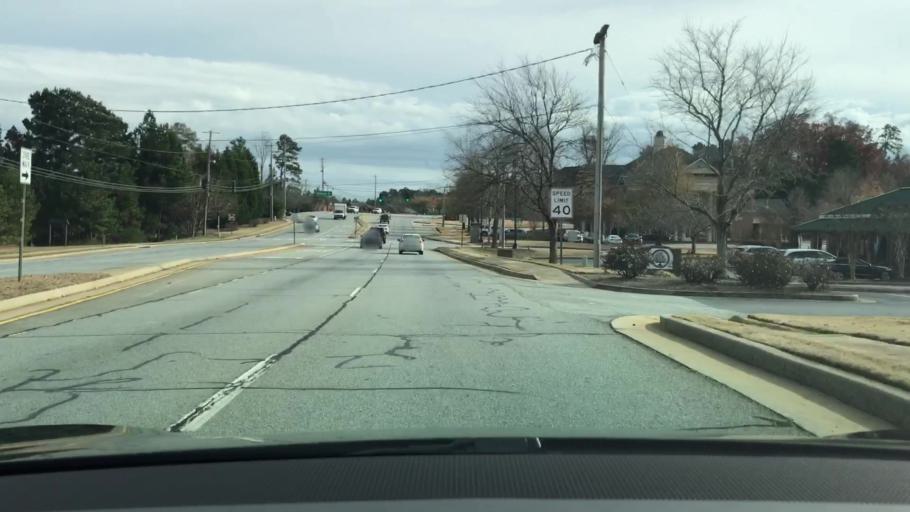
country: US
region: Georgia
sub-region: Gwinnett County
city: Buford
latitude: 34.1035
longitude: -84.0024
